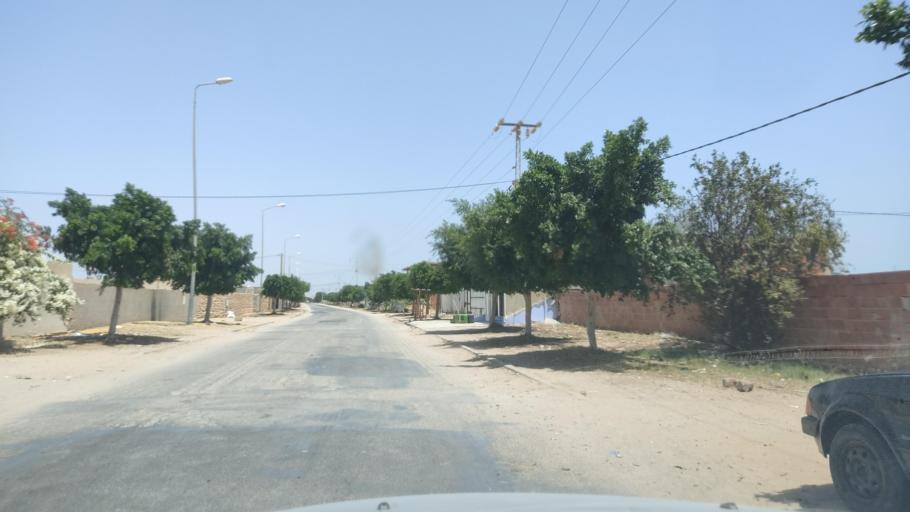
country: TN
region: Safaqis
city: Sfax
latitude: 34.6668
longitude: 10.7102
